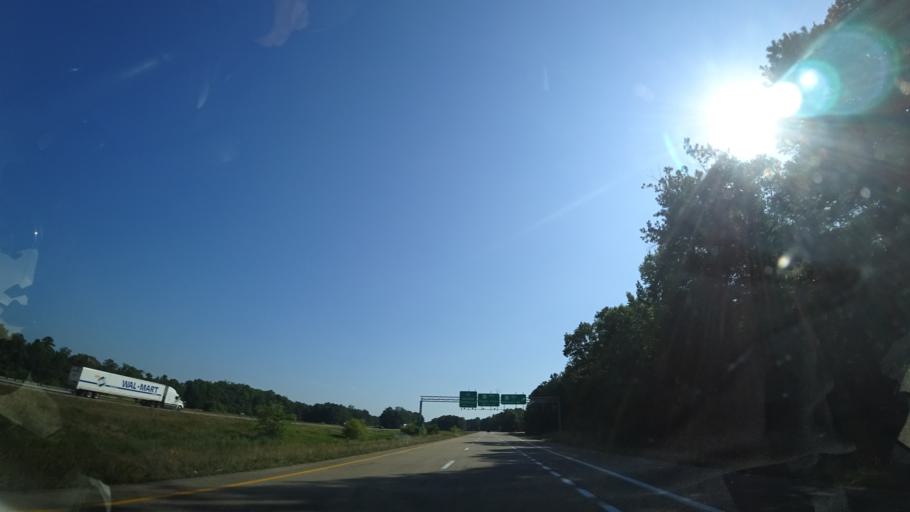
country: US
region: Virginia
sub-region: Henrico County
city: Sandston
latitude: 37.5041
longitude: -77.2787
